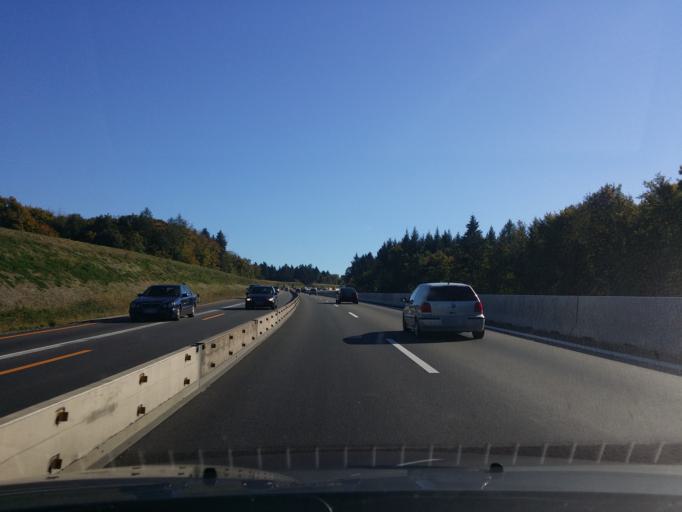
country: DE
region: Baden-Wuerttemberg
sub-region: Karlsruhe Region
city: Konigsbach-Stein
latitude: 48.9211
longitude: 8.6071
